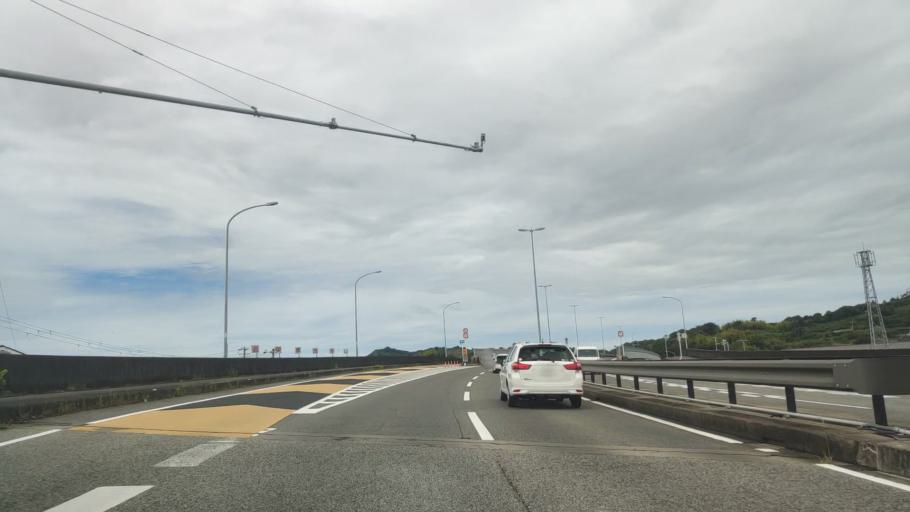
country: JP
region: Wakayama
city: Tanabe
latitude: 33.7413
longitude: 135.3883
